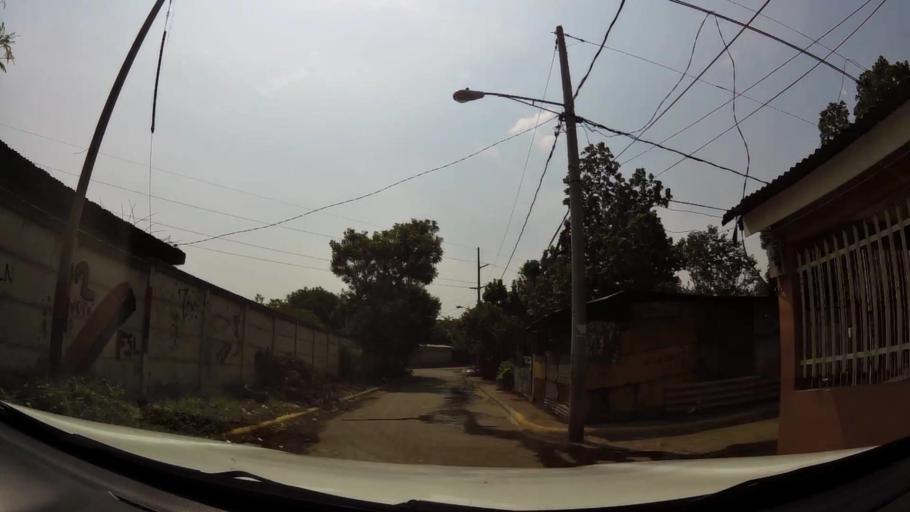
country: NI
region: Managua
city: Ciudad Sandino
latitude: 12.1255
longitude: -86.3167
